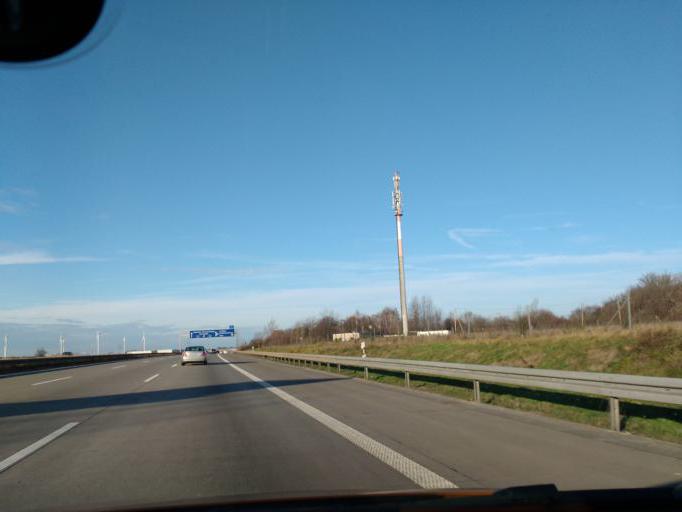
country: DE
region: Saxony-Anhalt
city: Hohenwarsleben
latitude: 52.1675
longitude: 11.5026
